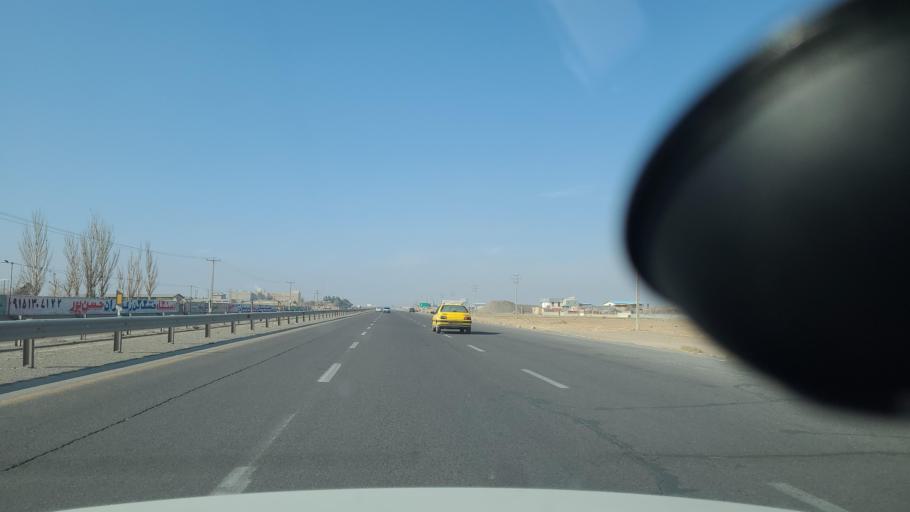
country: IR
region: Razavi Khorasan
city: Fariman
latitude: 35.7104
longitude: 59.8294
